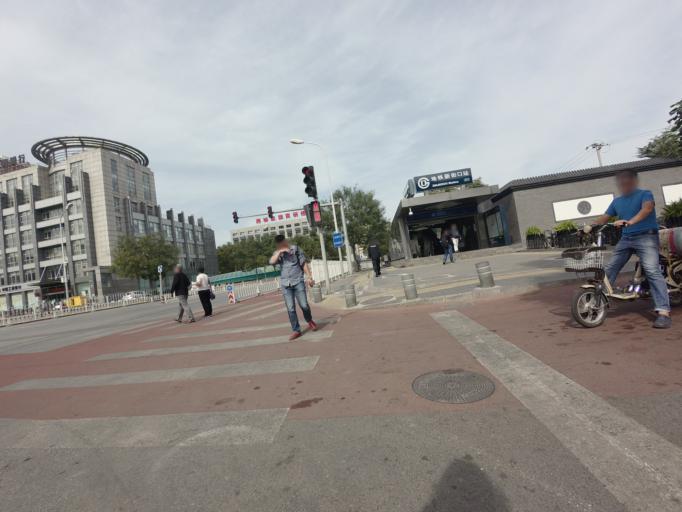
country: CN
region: Beijing
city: Jinrongjie
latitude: 39.9393
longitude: 116.3626
